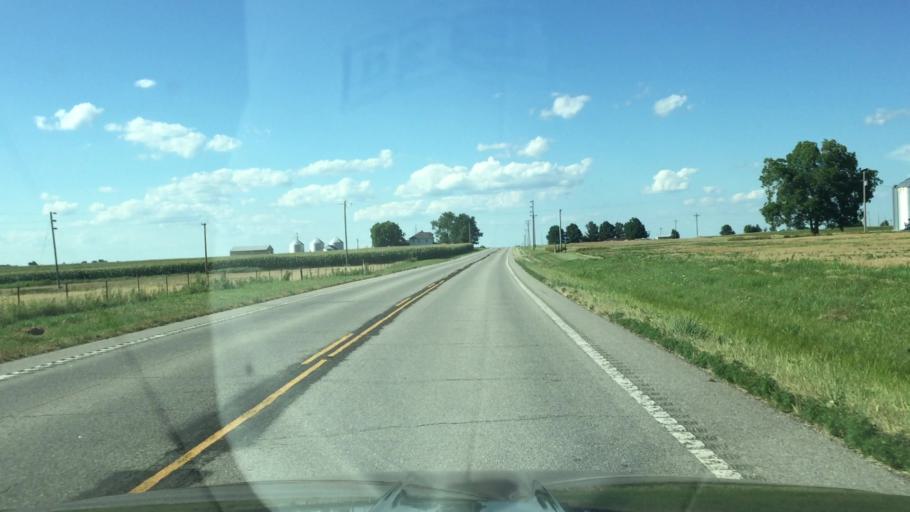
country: US
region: Missouri
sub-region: Moniteau County
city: Tipton
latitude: 38.6088
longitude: -92.7903
